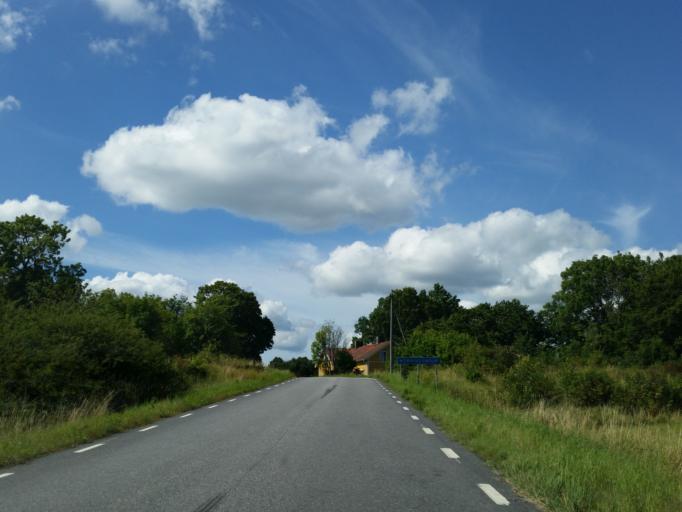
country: SE
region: Stockholm
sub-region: Sodertalje Kommun
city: Pershagen
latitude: 59.0499
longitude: 17.6756
